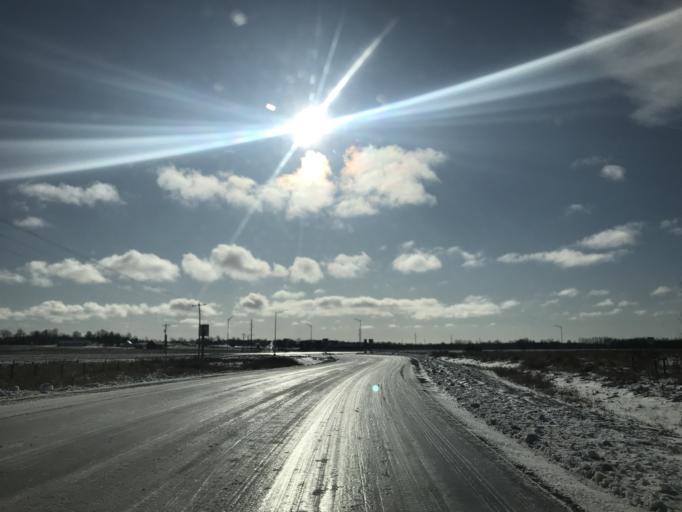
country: US
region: Wisconsin
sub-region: Kewaunee County
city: Luxemburg
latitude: 44.7188
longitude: -87.6208
